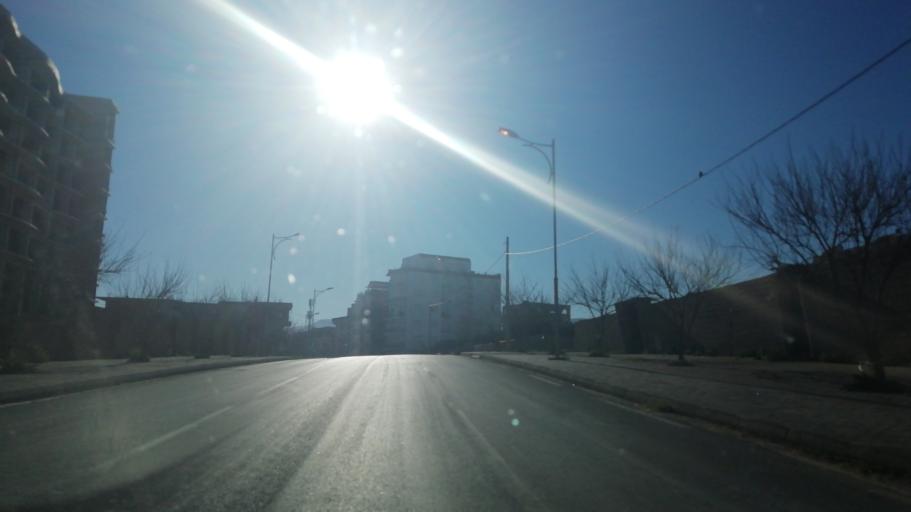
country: DZ
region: Oran
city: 'Ain el Turk
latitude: 35.7540
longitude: -0.7850
